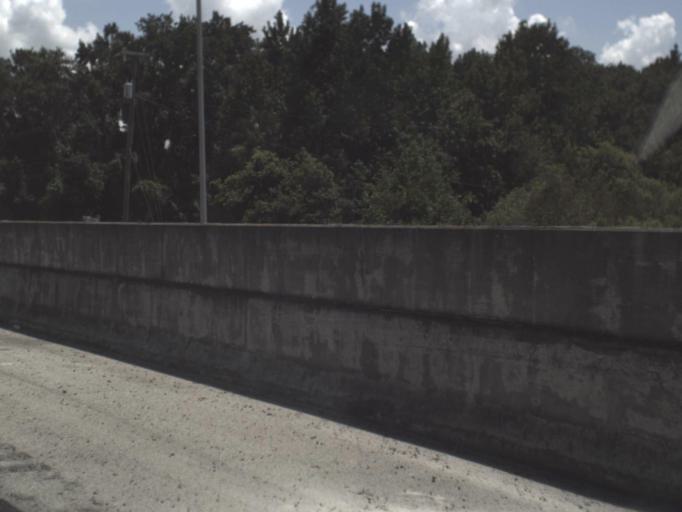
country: US
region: Florida
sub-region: Hillsborough County
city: Plant City
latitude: 28.0366
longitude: -82.1180
